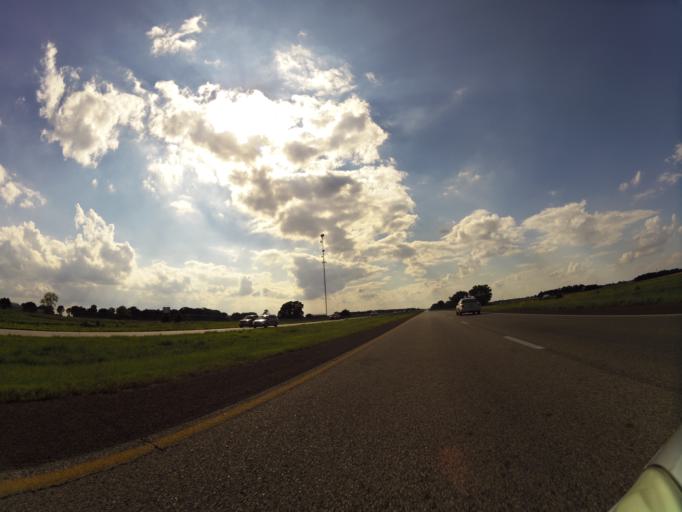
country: US
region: Kansas
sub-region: Reno County
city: Haven
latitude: 37.9089
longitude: -97.8062
